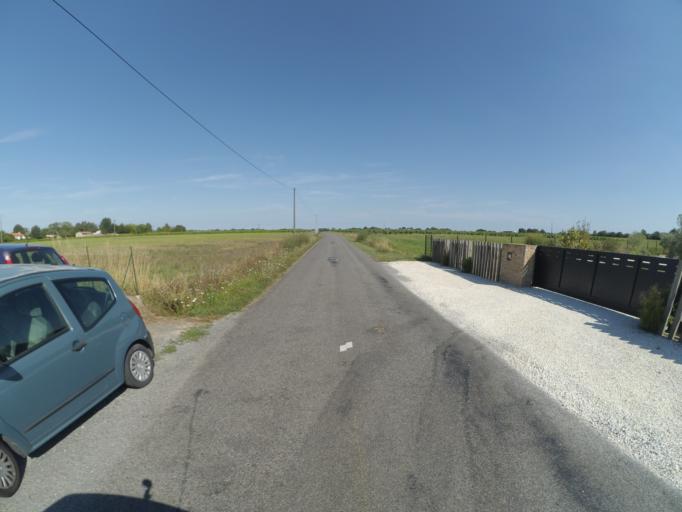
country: FR
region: Pays de la Loire
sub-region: Departement de la Loire-Atlantique
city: Le Pallet
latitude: 47.1587
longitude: -1.3240
